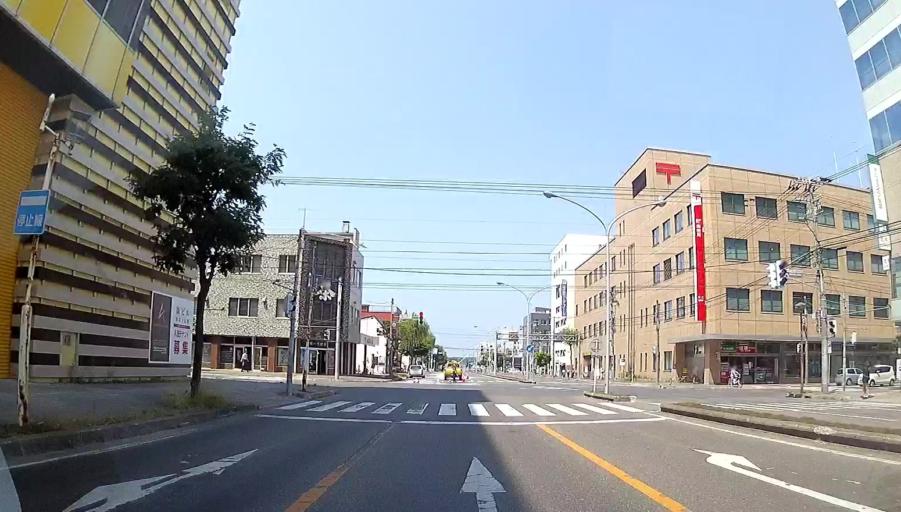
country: JP
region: Hokkaido
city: Obihiro
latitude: 42.9220
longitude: 143.2005
